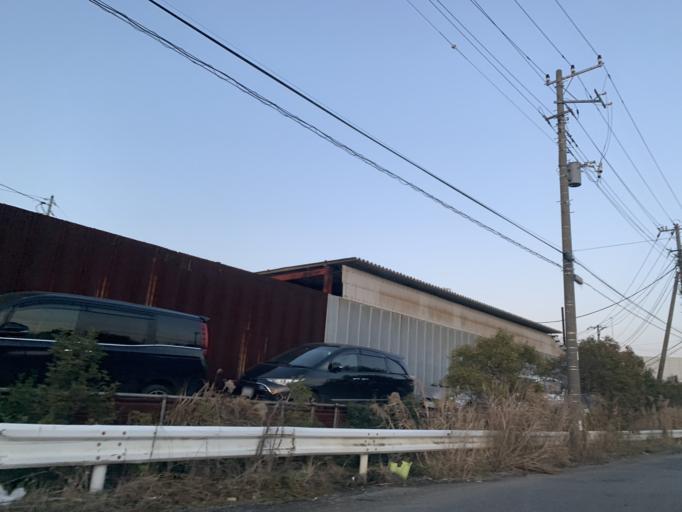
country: JP
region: Chiba
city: Funabashi
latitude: 35.6938
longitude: 139.9386
